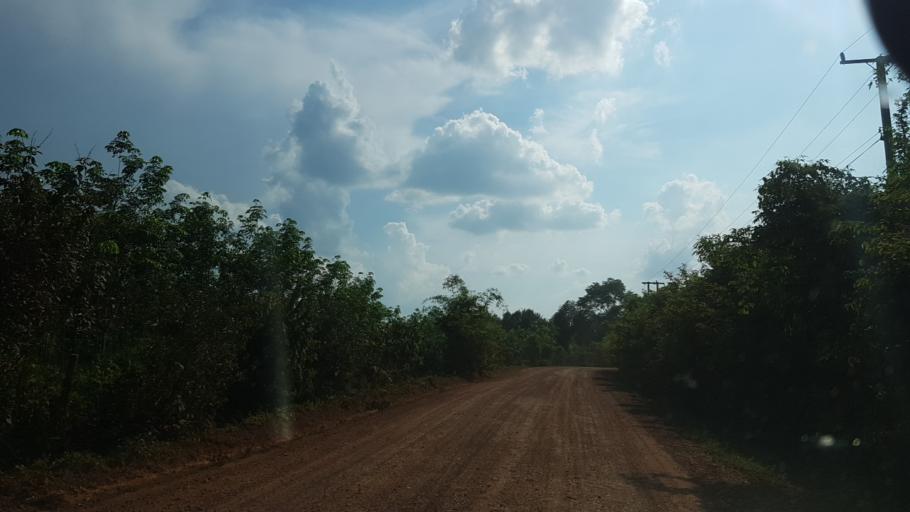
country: LA
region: Vientiane
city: Muang Phon-Hong
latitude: 18.3437
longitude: 102.2962
